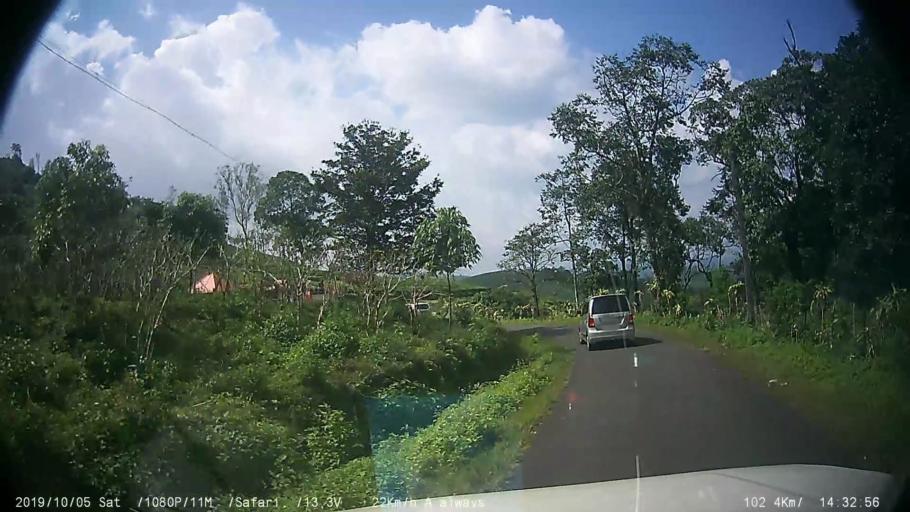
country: IN
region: Kerala
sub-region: Kottayam
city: Erattupetta
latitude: 9.6136
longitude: 76.9677
